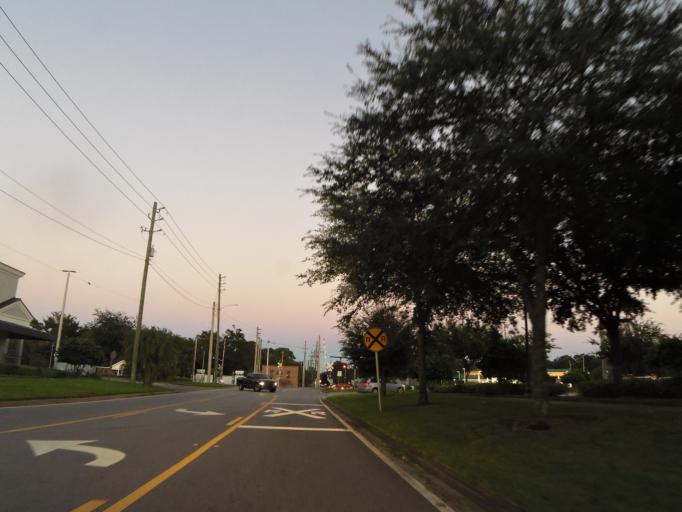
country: US
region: Florida
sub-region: Duval County
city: Jacksonville
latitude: 30.2885
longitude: -81.7216
